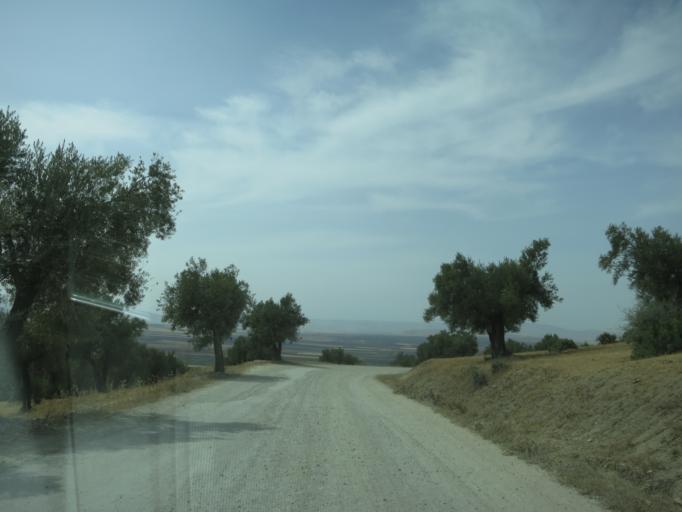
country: MA
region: Meknes-Tafilalet
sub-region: Meknes
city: Meknes
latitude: 34.0621
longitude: -5.5291
